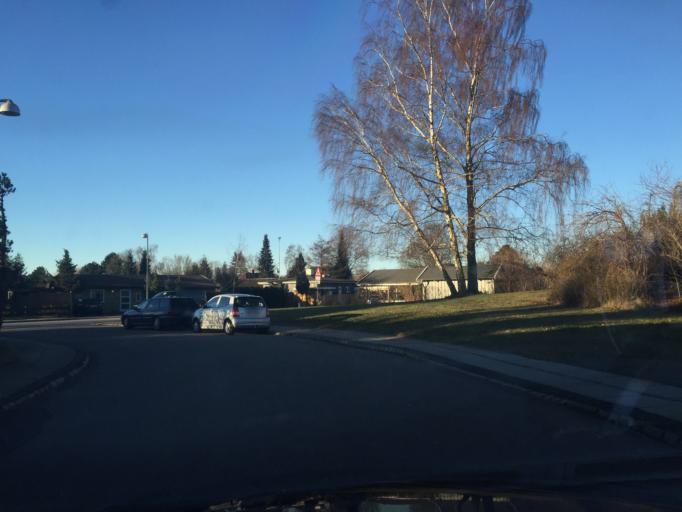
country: DK
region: Capital Region
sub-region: Fureso Kommune
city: Vaerlose
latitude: 55.7579
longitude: 12.4029
